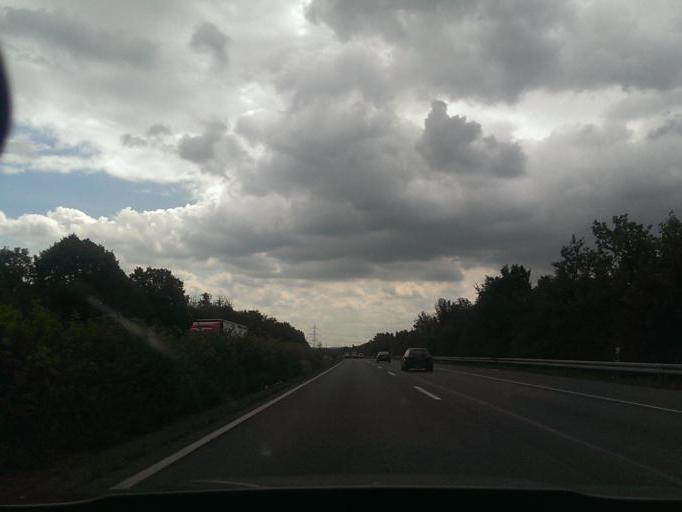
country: DE
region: North Rhine-Westphalia
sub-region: Regierungsbezirk Detmold
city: Paderborn
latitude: 51.7135
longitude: 8.7048
